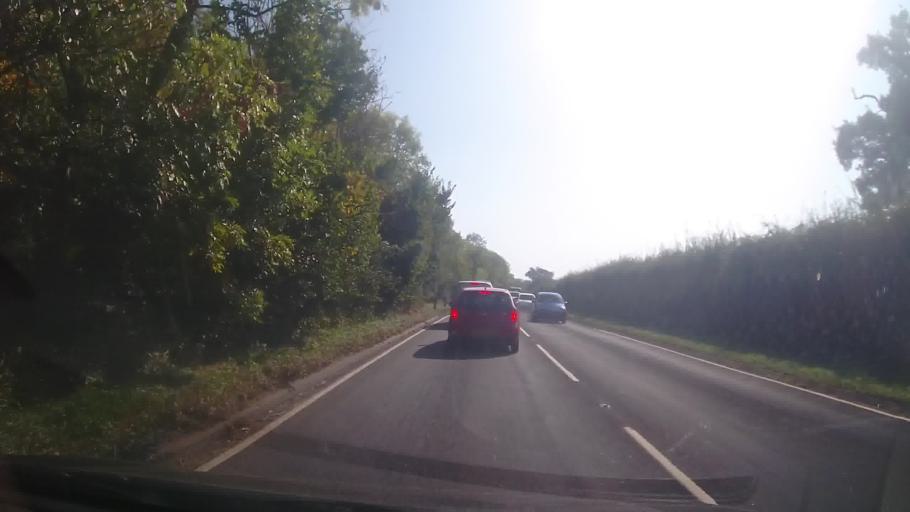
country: GB
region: England
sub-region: Worcestershire
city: Evesham
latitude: 52.1236
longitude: -1.9819
